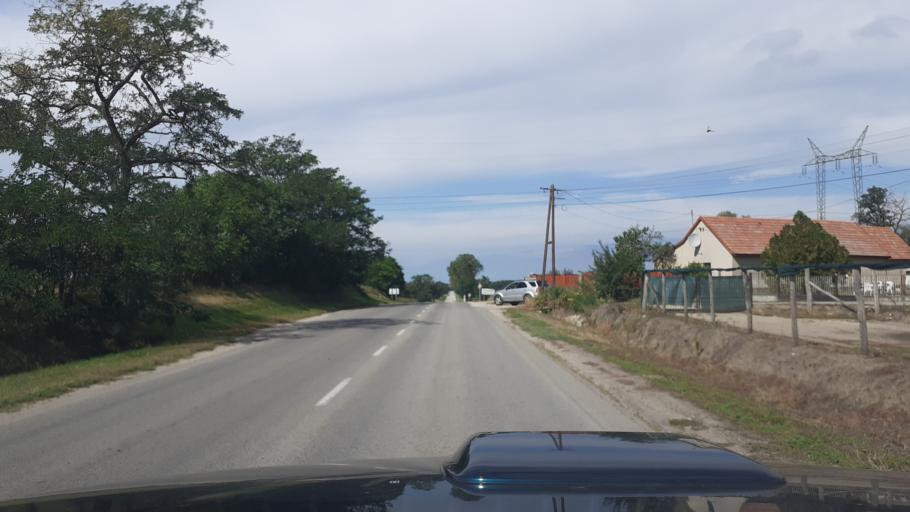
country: HU
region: Fejer
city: Seregelyes
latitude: 47.1096
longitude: 18.6129
